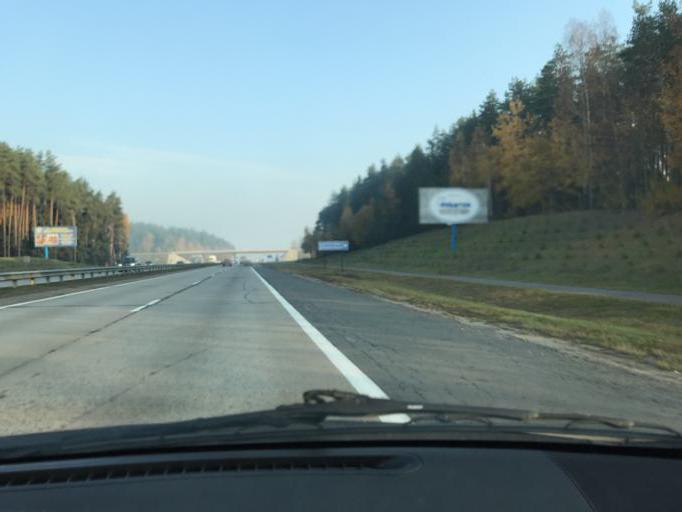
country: BY
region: Minsk
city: Borovlyany
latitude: 54.0003
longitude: 27.6572
